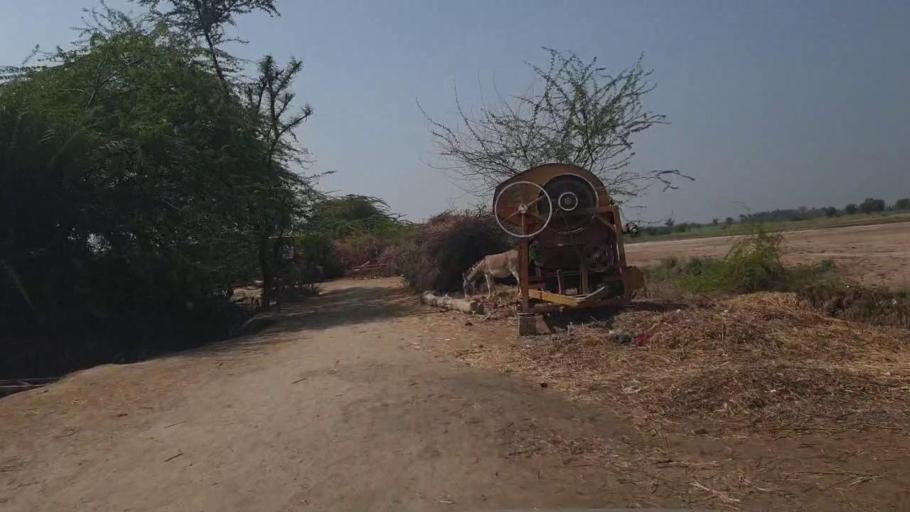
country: PK
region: Sindh
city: Dhoro Naro
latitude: 25.4645
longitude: 69.6128
